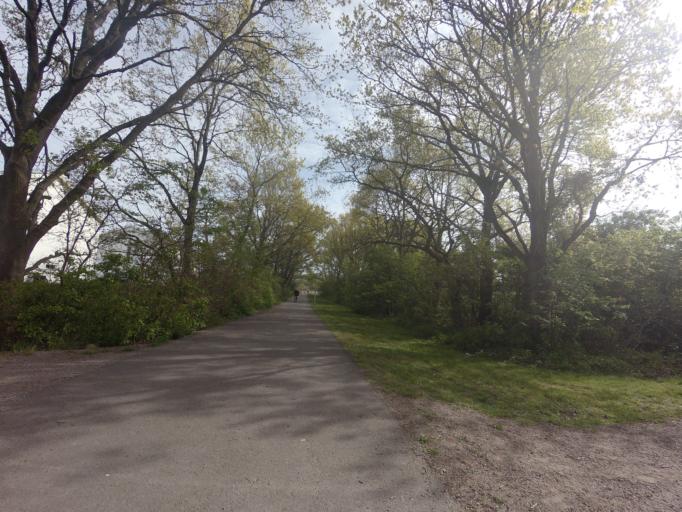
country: SE
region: Skane
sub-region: Hoganas Kommun
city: Hoganas
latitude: 56.1942
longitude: 12.5807
